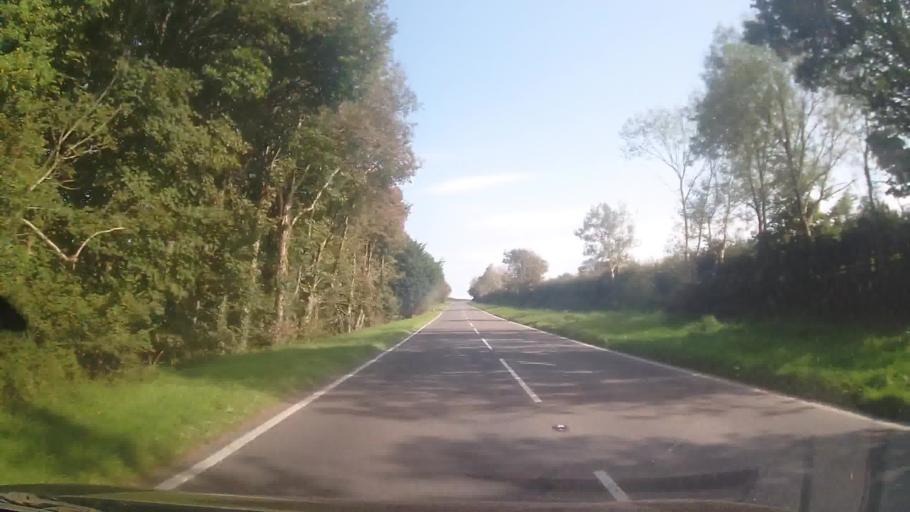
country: GB
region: Wales
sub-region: Pembrokeshire
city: Nevern
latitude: 52.0126
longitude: -4.7529
